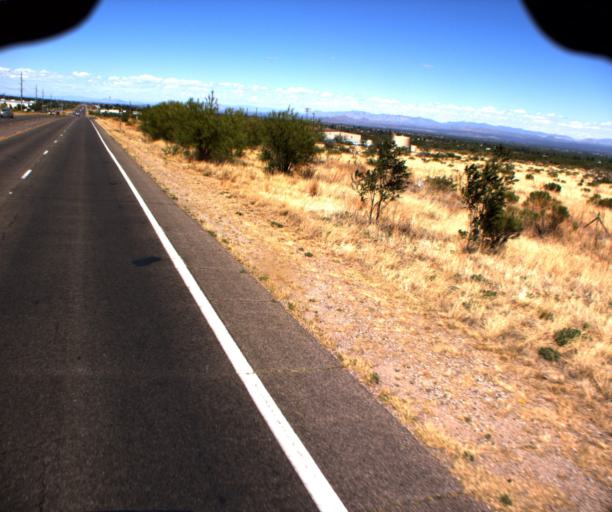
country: US
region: Arizona
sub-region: Cochise County
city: Sierra Vista Southeast
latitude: 31.4563
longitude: -110.2574
